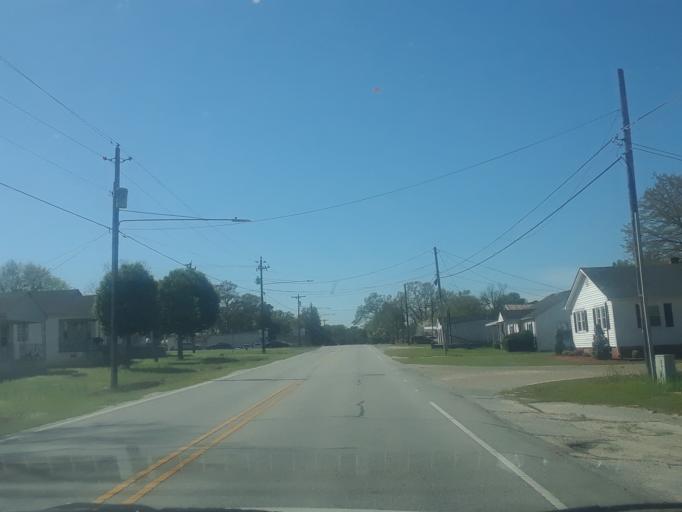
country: US
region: North Carolina
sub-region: Harnett County
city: Erwin
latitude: 35.3167
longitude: -78.6474
